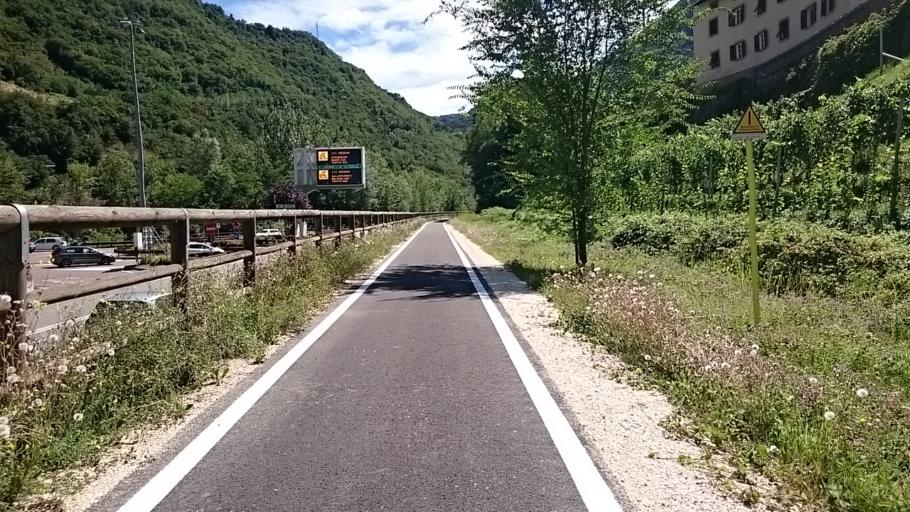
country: IT
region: Trentino-Alto Adige
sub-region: Bolzano
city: Cornedo All'Isarco
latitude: 46.4931
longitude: 11.4110
